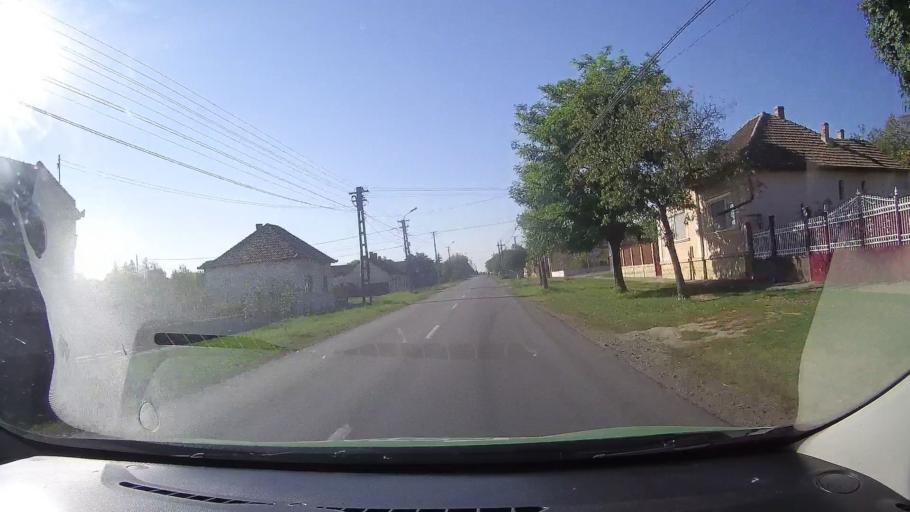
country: RO
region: Satu Mare
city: Carei
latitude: 47.6755
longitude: 22.4689
